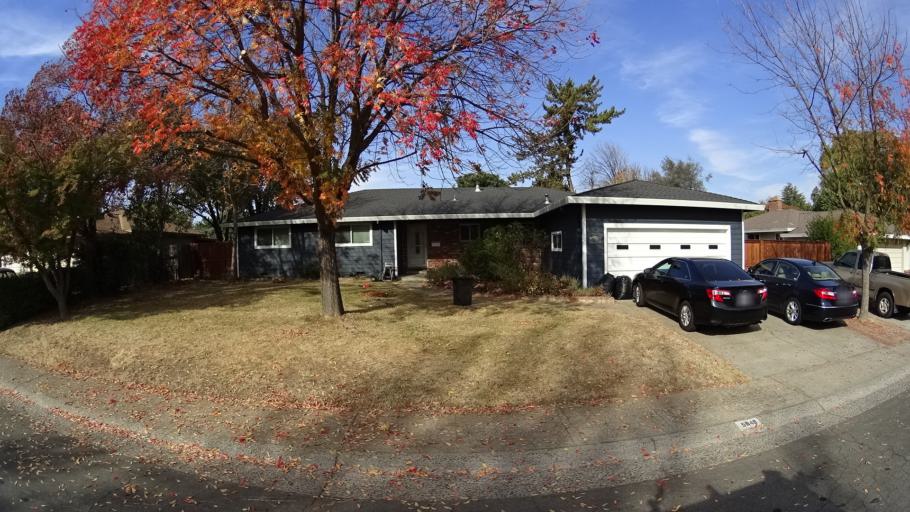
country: US
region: California
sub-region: Sacramento County
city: Fair Oaks
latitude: 38.6683
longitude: -121.2781
